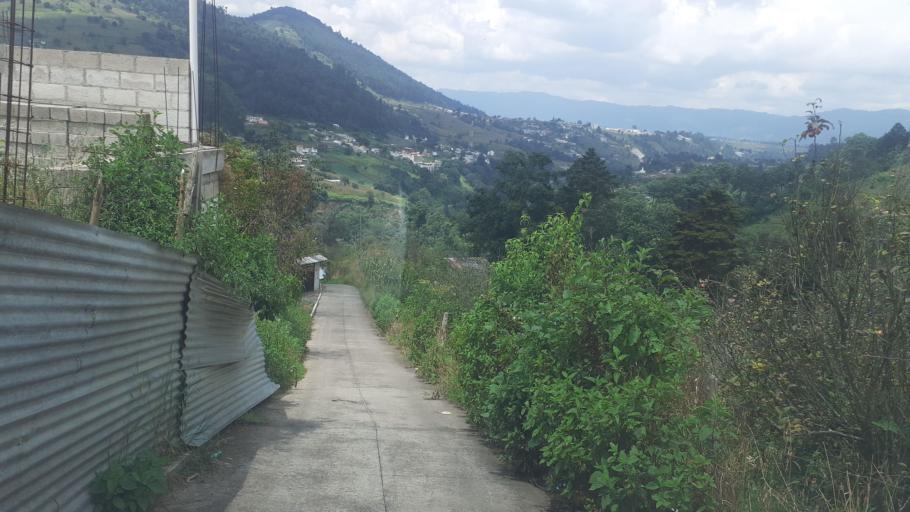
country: GT
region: Quetzaltenango
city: Cantel
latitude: 14.8188
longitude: -91.4496
